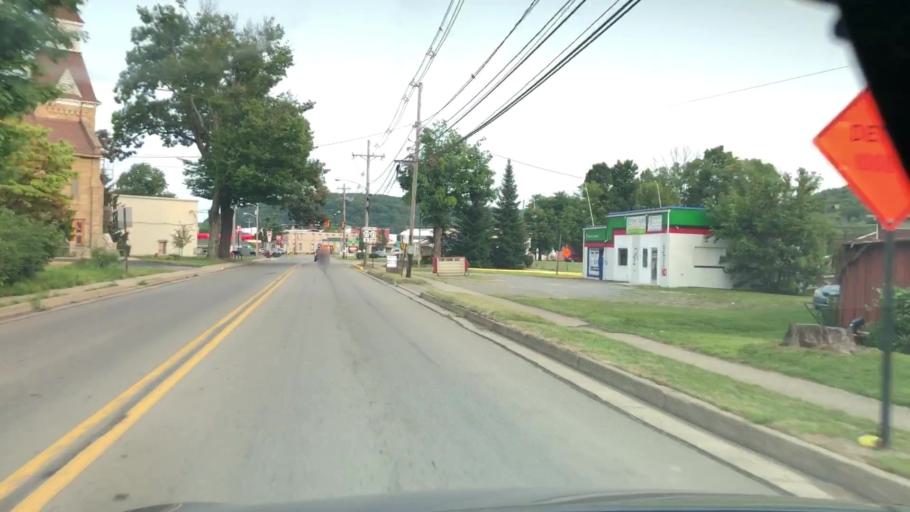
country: US
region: Pennsylvania
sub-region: Crawford County
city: Titusville
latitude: 41.6278
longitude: -79.6823
